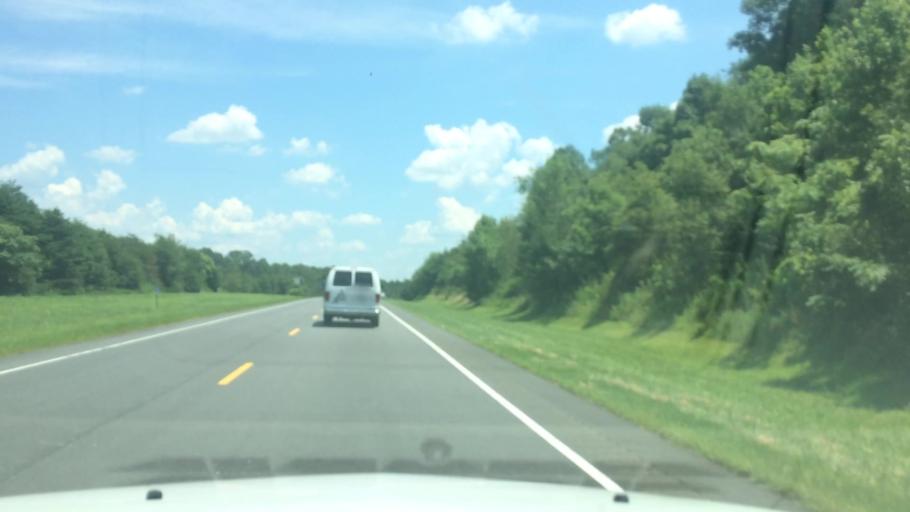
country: US
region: North Carolina
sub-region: Alexander County
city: Stony Point
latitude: 35.8154
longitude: -80.9892
